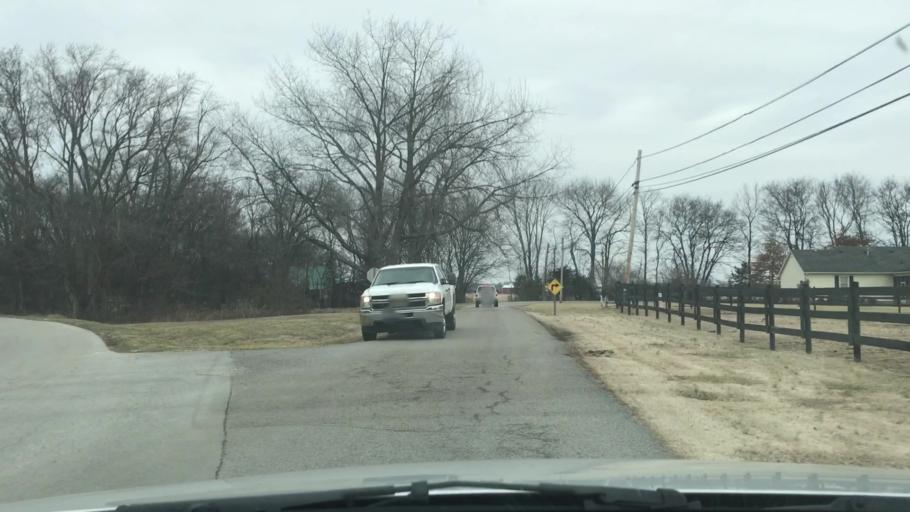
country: US
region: Kentucky
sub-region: Edmonson County
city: Brownsville
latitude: 37.0464
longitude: -86.2511
